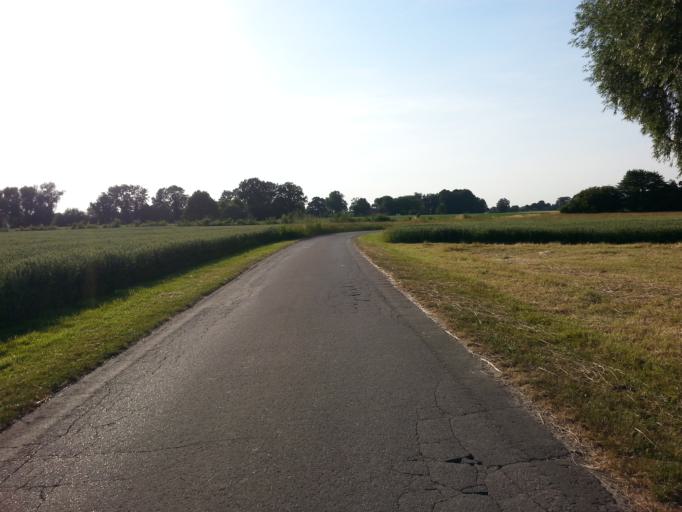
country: DE
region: North Rhine-Westphalia
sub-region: Regierungsbezirk Munster
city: Havixbeck
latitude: 51.9561
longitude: 7.4513
